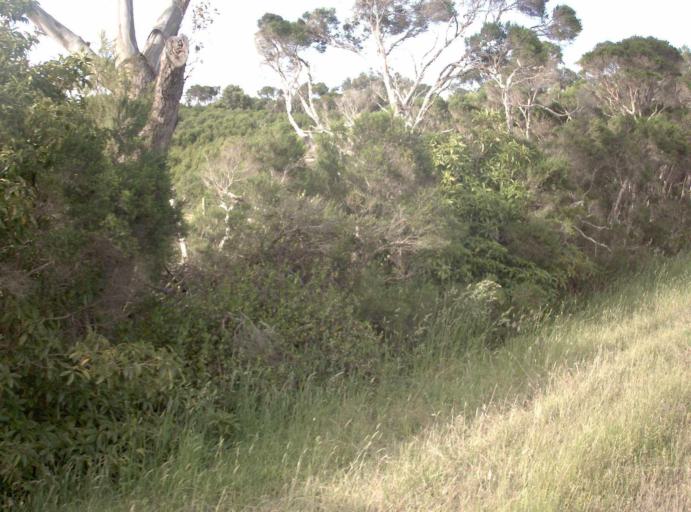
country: AU
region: Victoria
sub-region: Bass Coast
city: North Wonthaggi
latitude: -38.6001
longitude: 145.7775
